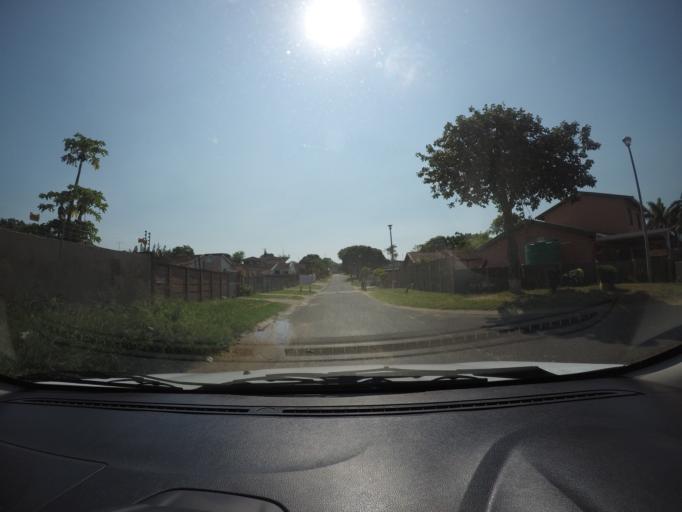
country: ZA
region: KwaZulu-Natal
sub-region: uThungulu District Municipality
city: Richards Bay
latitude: -28.7220
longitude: 32.0455
